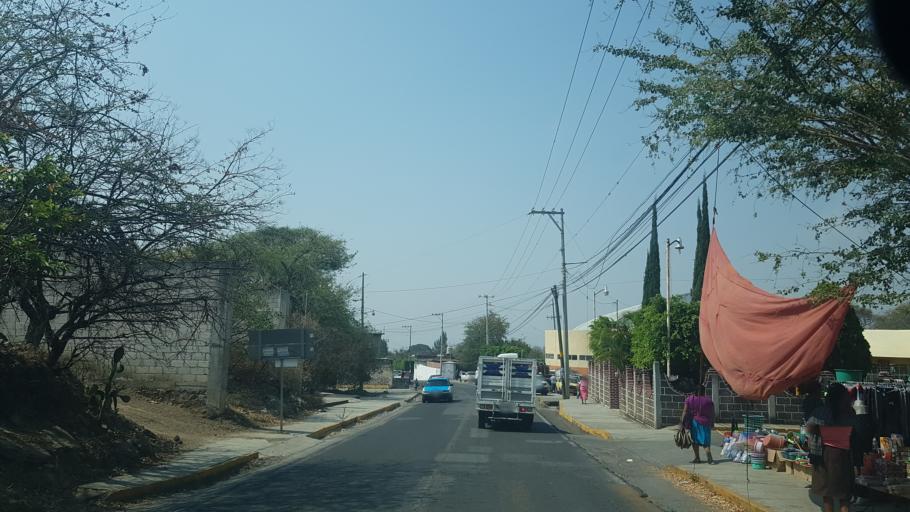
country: MX
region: Morelos
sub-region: Temoac
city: Temoac
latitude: 18.7707
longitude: -98.7786
